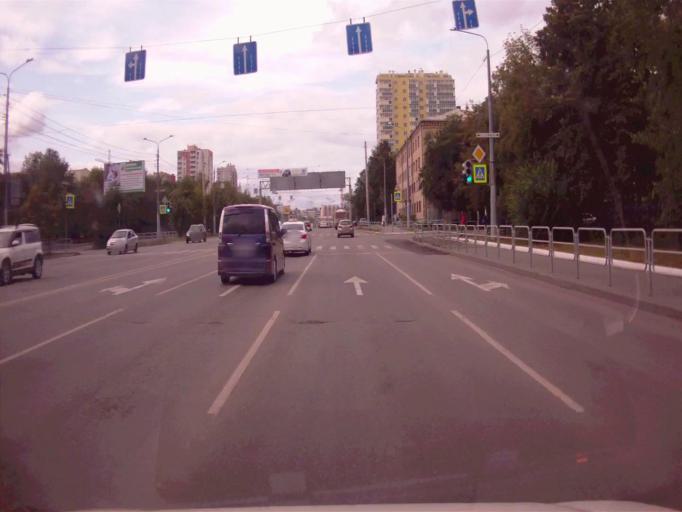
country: RU
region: Chelyabinsk
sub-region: Gorod Chelyabinsk
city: Chelyabinsk
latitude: 55.1431
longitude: 61.3901
